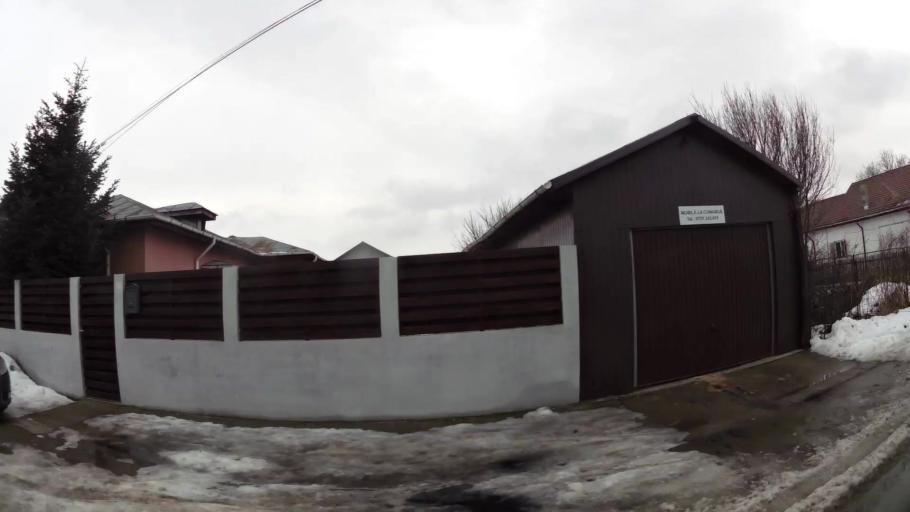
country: RO
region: Ilfov
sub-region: Comuna Tunari
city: Tunari
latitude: 44.5446
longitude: 26.1310
